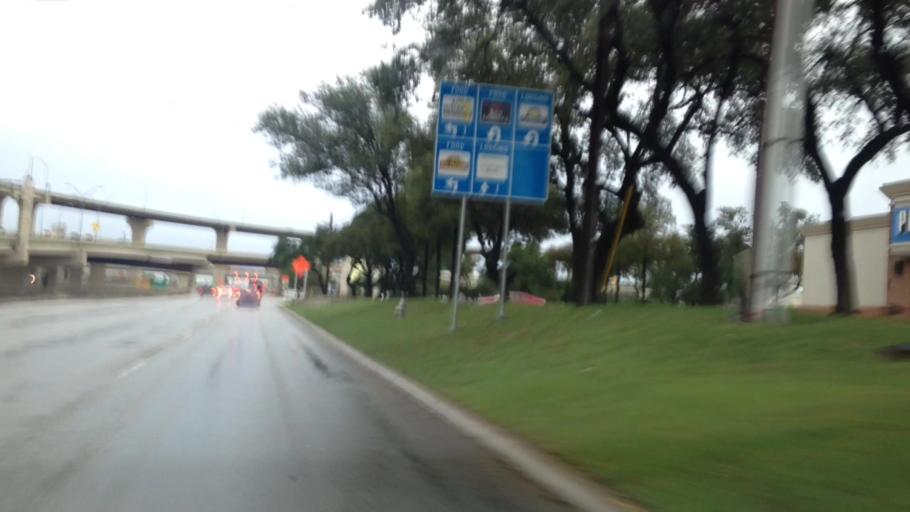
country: US
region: Texas
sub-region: Bexar County
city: Hollywood Park
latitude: 29.6055
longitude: -98.4691
